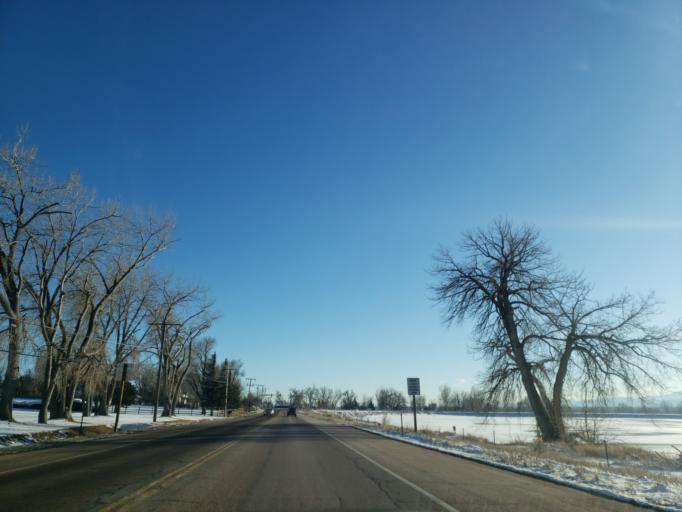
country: US
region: Colorado
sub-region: Larimer County
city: Fort Collins
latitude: 40.6203
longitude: -105.0723
